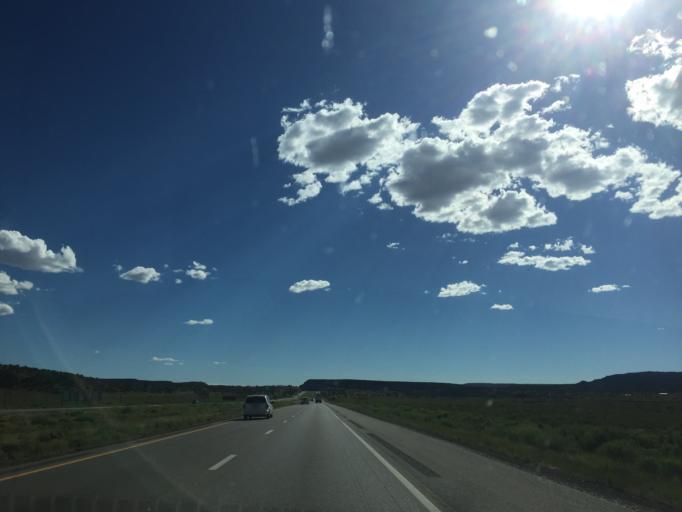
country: US
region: New Mexico
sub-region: McKinley County
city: Gallup
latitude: 35.4354
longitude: -108.9685
